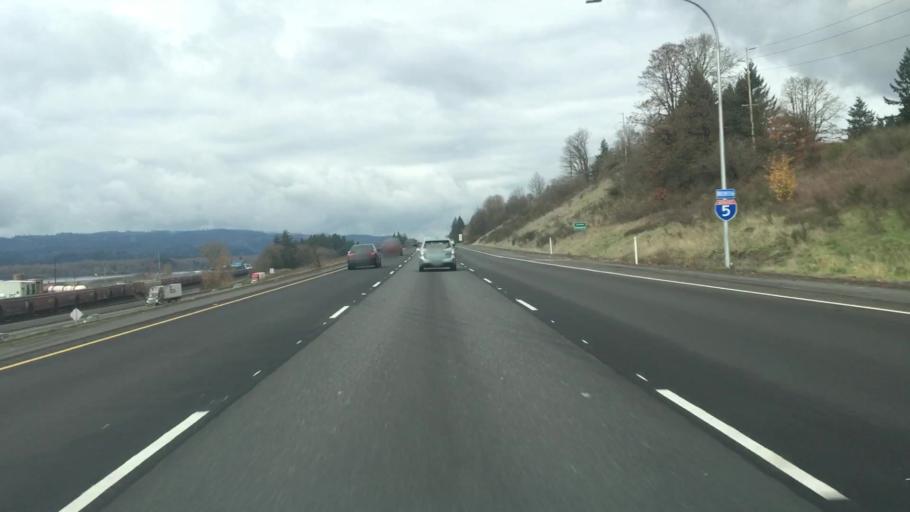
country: US
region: Washington
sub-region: Cowlitz County
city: Kalama
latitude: 45.9869
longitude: -122.8290
